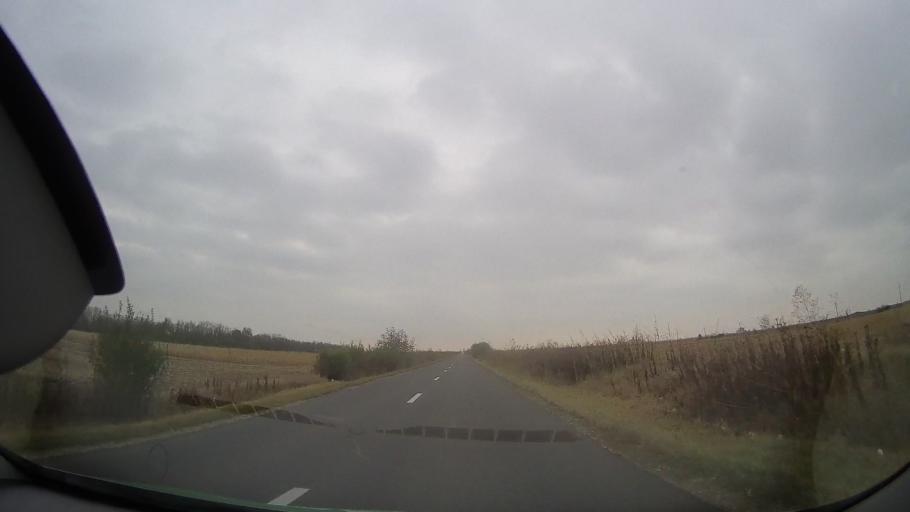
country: RO
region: Ialomita
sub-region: Comuna Manasia
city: Manasia
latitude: 44.7337
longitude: 26.7013
